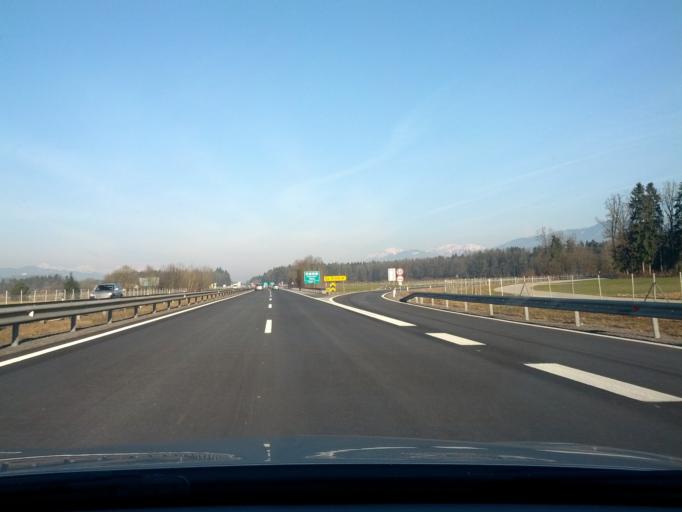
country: SI
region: Sencur
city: Sencur
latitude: 46.2179
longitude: 14.4406
